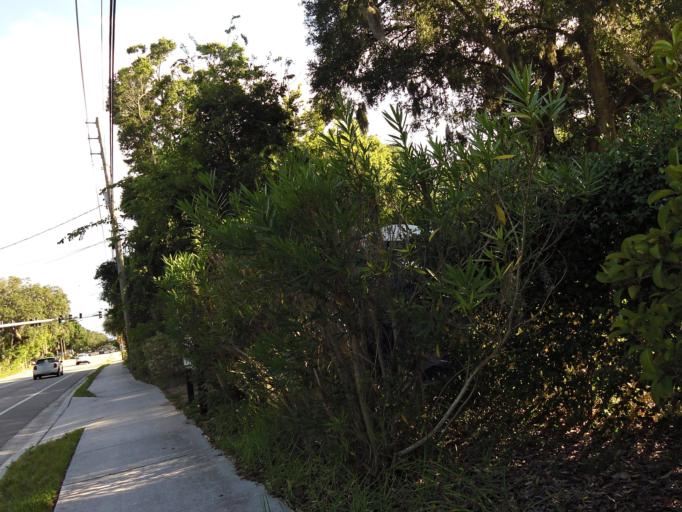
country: US
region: Florida
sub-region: Nassau County
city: Fernandina Beach
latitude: 30.6680
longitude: -81.4518
